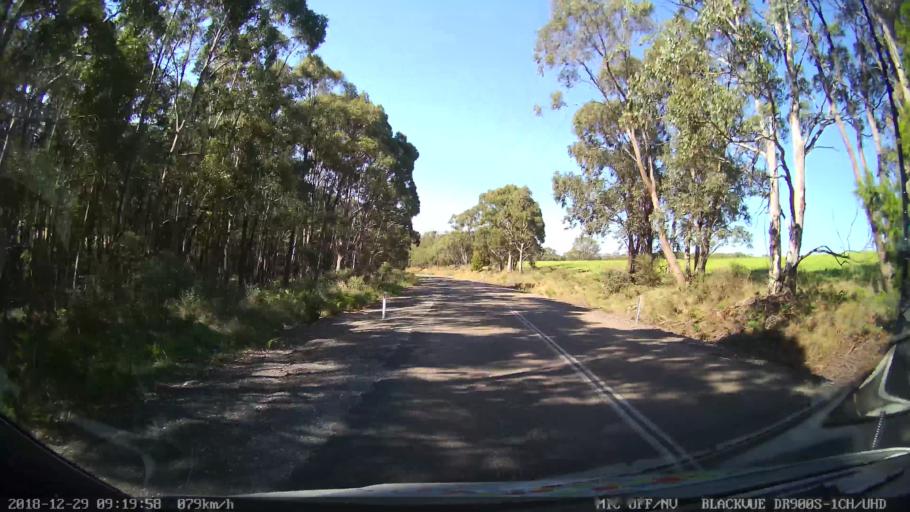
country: AU
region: New South Wales
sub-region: Upper Lachlan Shire
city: Crookwell
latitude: -34.4866
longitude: 149.4248
